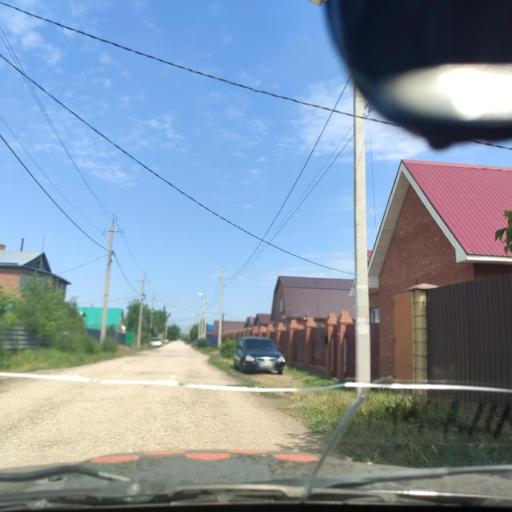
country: RU
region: Samara
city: Tol'yatti
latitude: 53.5732
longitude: 49.4077
